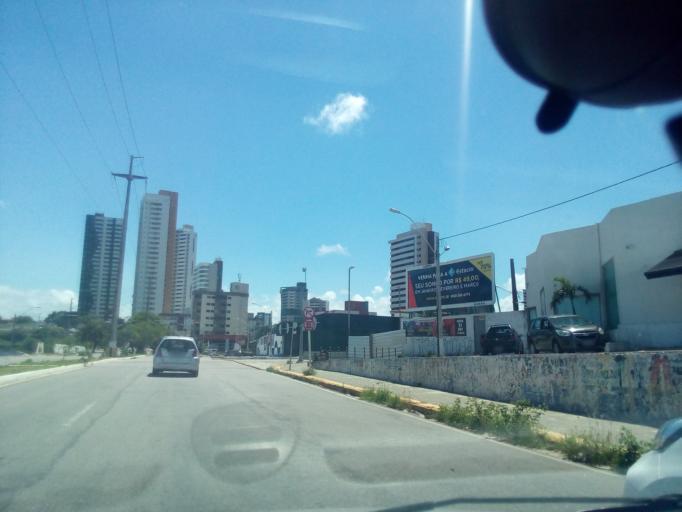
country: BR
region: Rio Grande do Norte
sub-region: Natal
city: Natal
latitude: -5.8269
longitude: -35.2167
